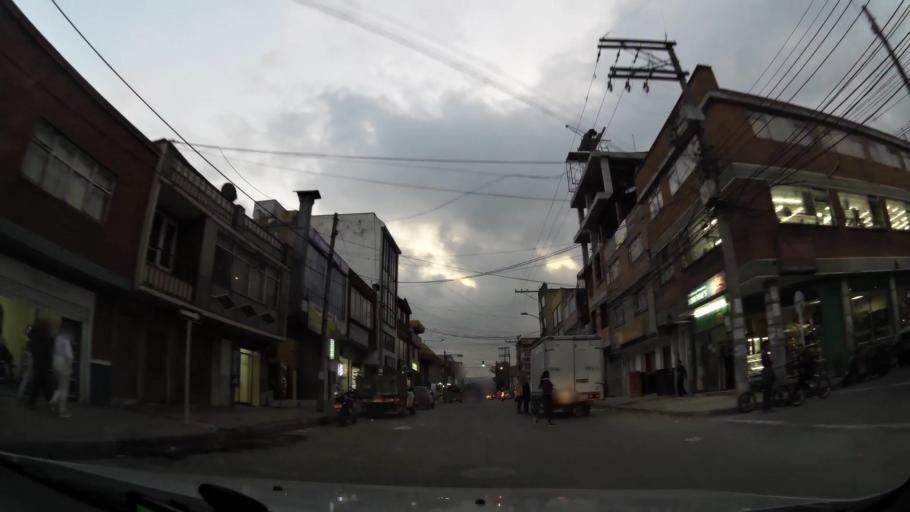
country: CO
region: Bogota D.C.
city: Bogota
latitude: 4.5838
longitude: -74.1250
